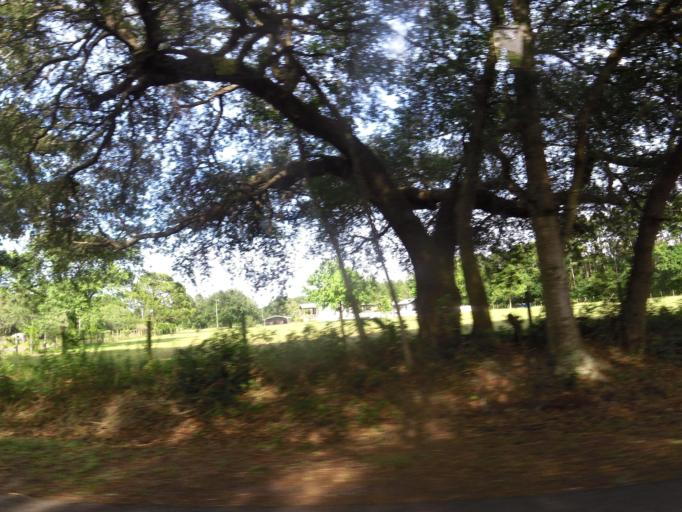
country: US
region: Florida
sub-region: Nassau County
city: Fernandina Beach
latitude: 30.5219
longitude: -81.4930
